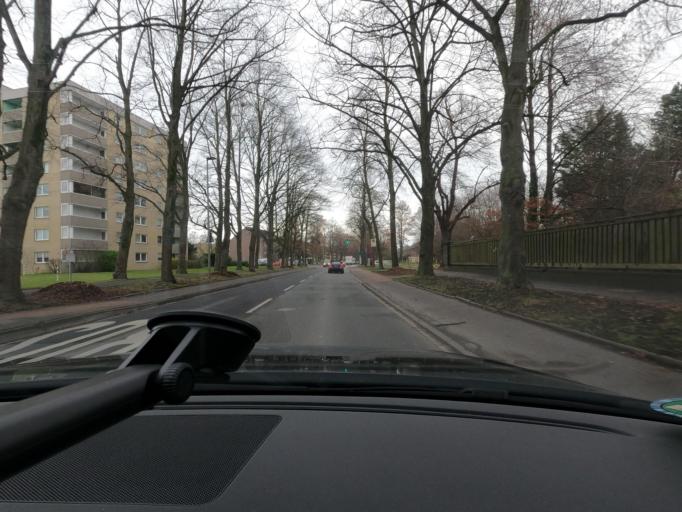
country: DE
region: North Rhine-Westphalia
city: Tonisvorst
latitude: 51.3406
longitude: 6.5302
